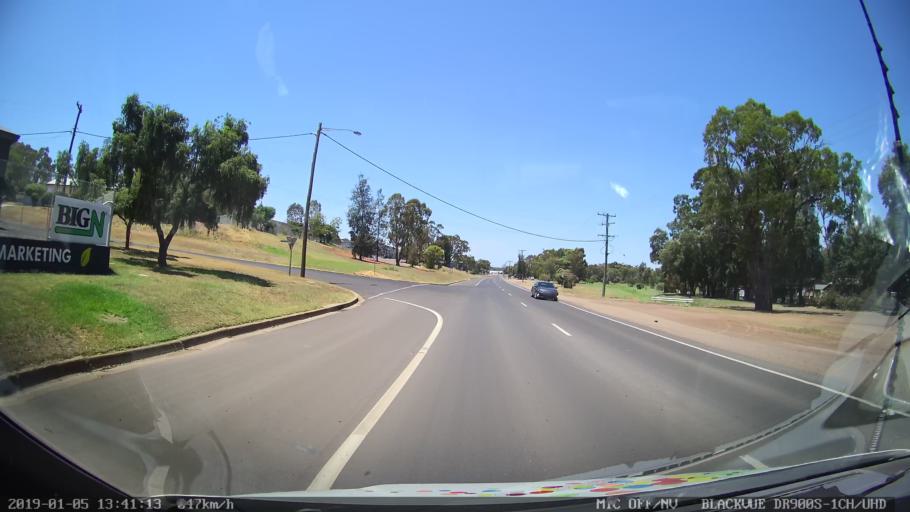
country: AU
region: New South Wales
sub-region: Gunnedah
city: Gunnedah
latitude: -30.9793
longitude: 150.2373
